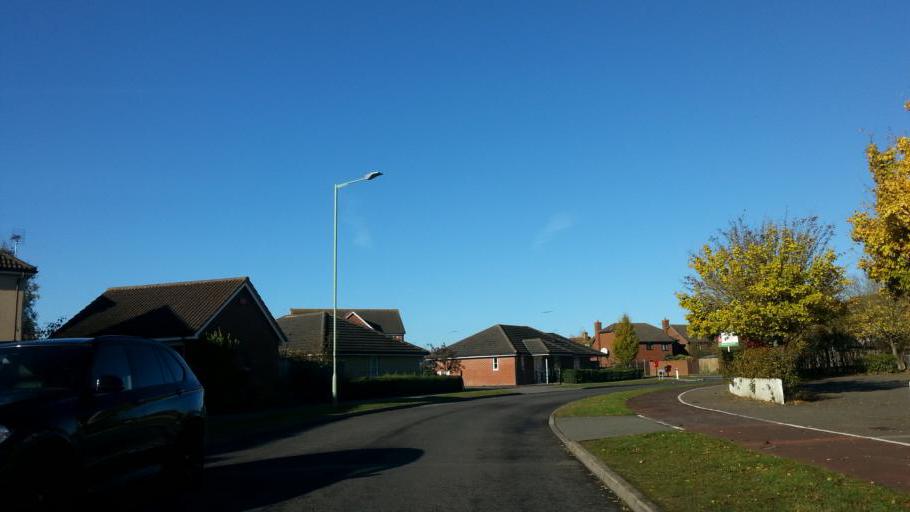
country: GB
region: England
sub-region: Suffolk
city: Kesgrave
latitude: 52.0595
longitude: 1.2529
